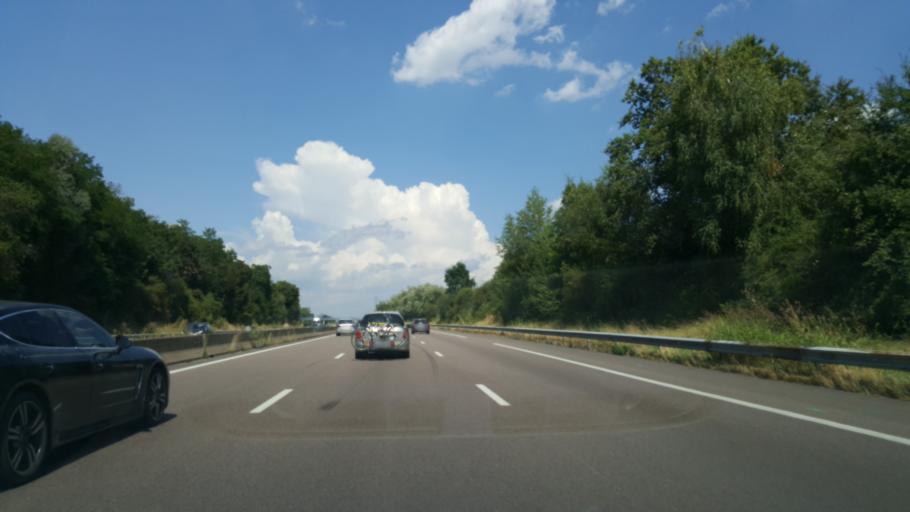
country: FR
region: Bourgogne
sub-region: Departement de Saone-et-Loire
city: Tournus
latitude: 46.5243
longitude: 4.9175
